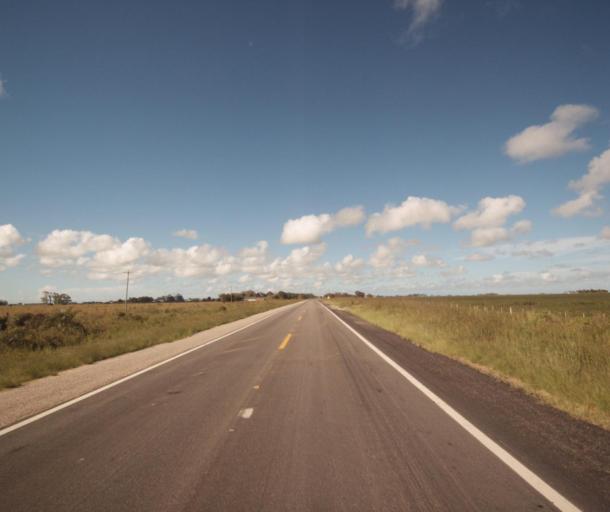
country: UY
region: Cerro Largo
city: Rio Branco
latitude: -33.0402
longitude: -52.8618
